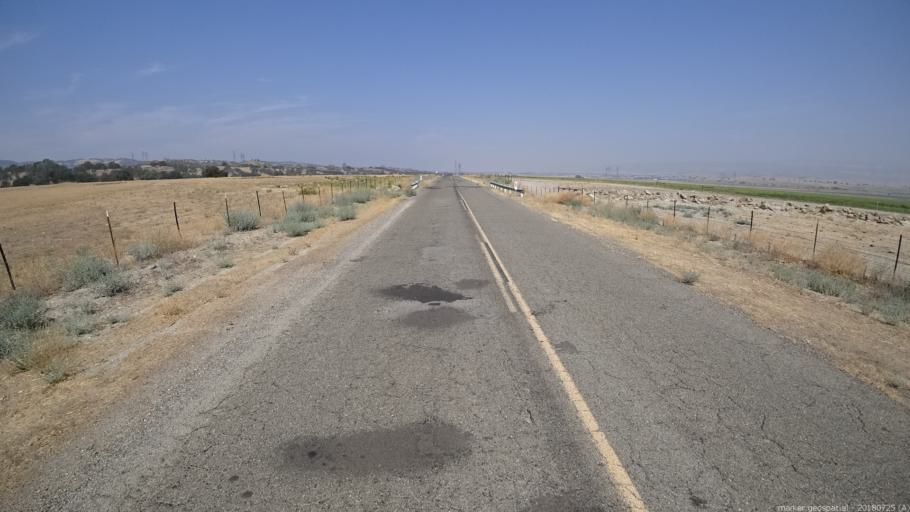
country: US
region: California
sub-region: San Luis Obispo County
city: Shandon
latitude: 35.8130
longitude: -120.3748
